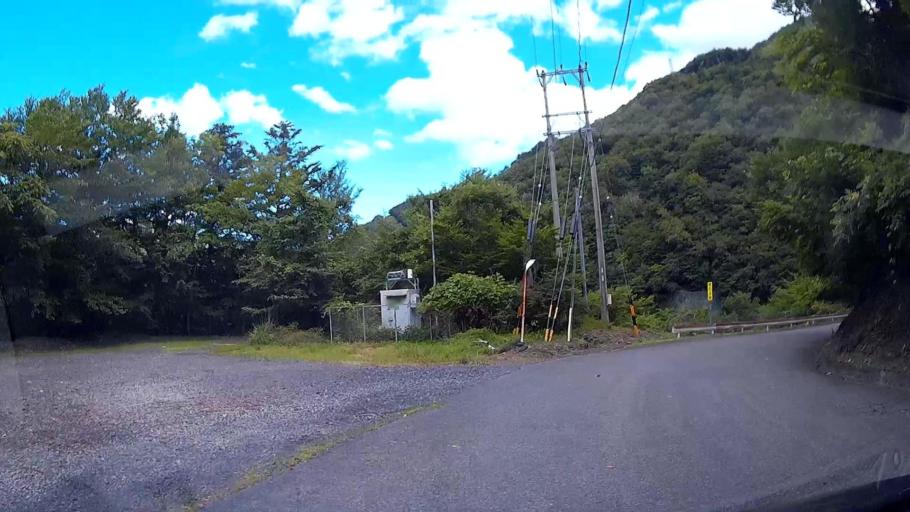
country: JP
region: Shizuoka
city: Shizuoka-shi
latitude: 35.3113
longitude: 138.1874
